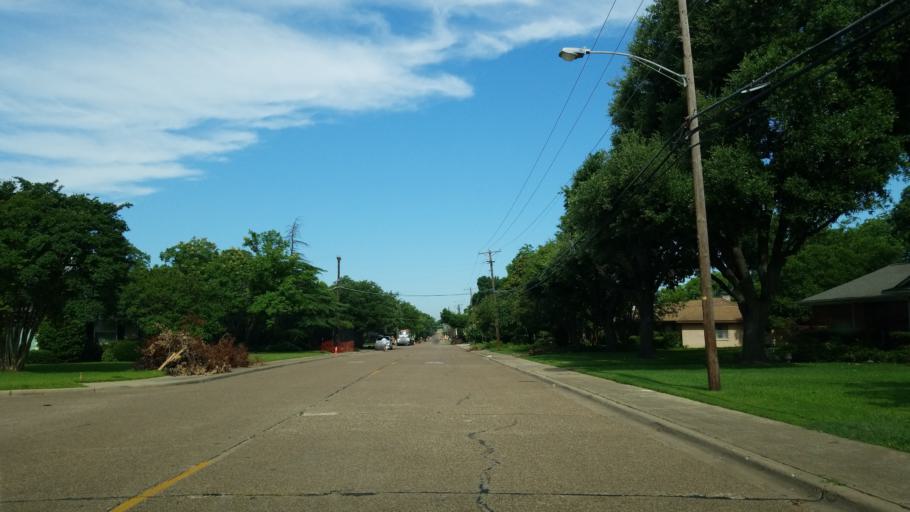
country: US
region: Texas
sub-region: Dallas County
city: Farmers Branch
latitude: 32.9023
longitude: -96.8419
